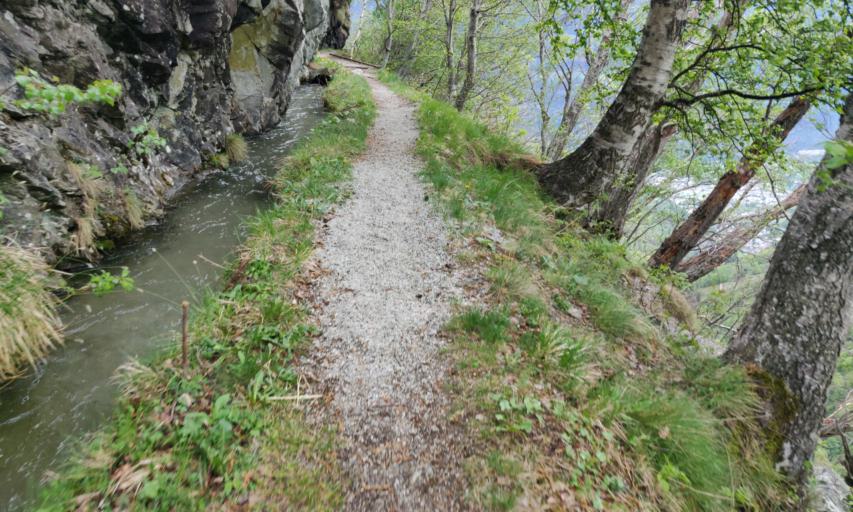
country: CH
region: Valais
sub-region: Visp District
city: Baltschieder
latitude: 46.3191
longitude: 7.8833
